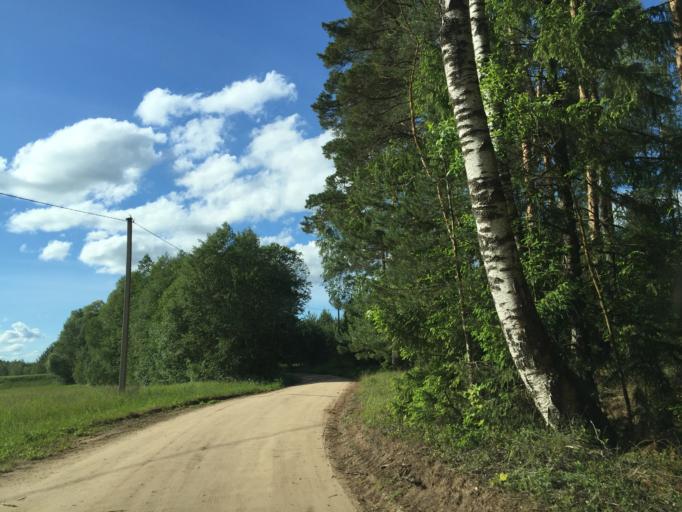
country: LV
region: Vecumnieki
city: Vecumnieki
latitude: 56.4437
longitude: 24.5801
